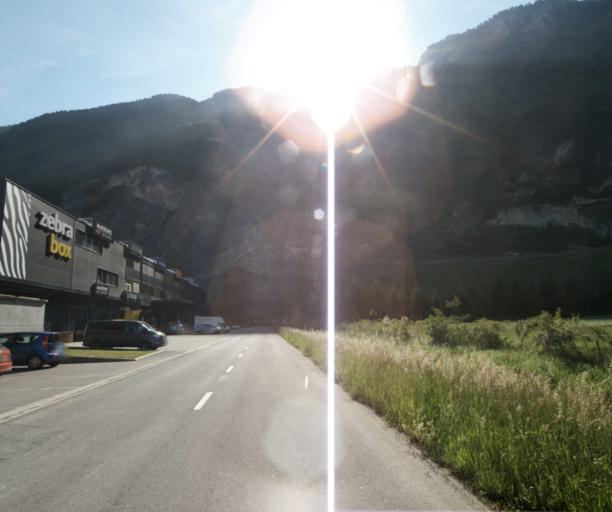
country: CH
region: Vaud
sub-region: Aigle District
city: Villeneuve
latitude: 46.3851
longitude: 6.9345
